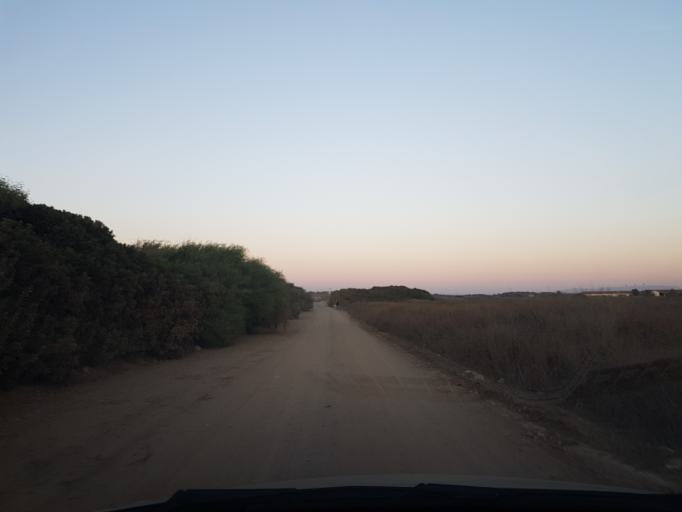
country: IT
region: Sardinia
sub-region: Provincia di Oristano
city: Riola Sardo
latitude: 40.0411
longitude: 8.3987
